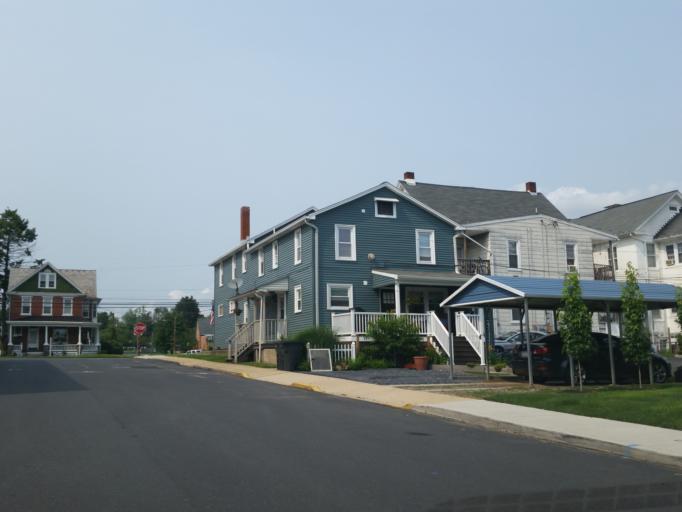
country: US
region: Pennsylvania
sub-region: Cumberland County
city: Camp Hill
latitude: 40.2397
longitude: -76.9228
